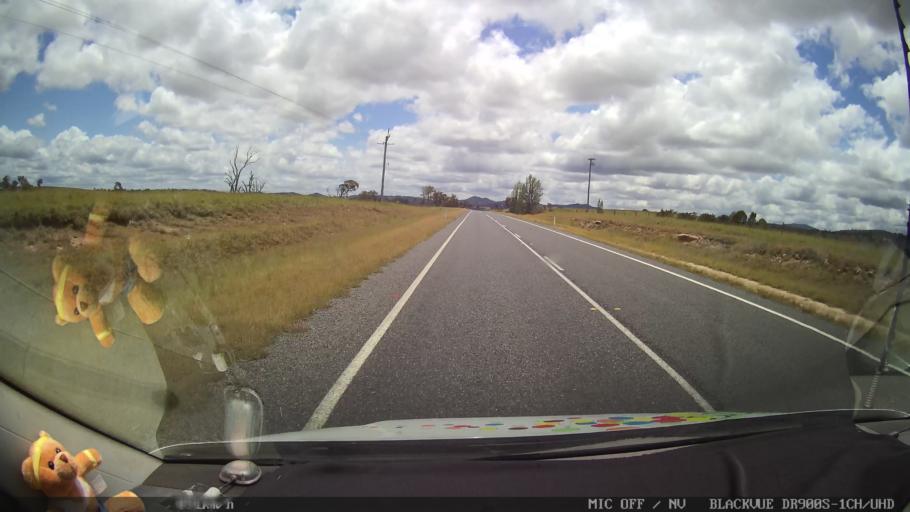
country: AU
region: New South Wales
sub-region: Glen Innes Severn
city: Glen Innes
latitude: -29.4156
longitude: 151.8647
